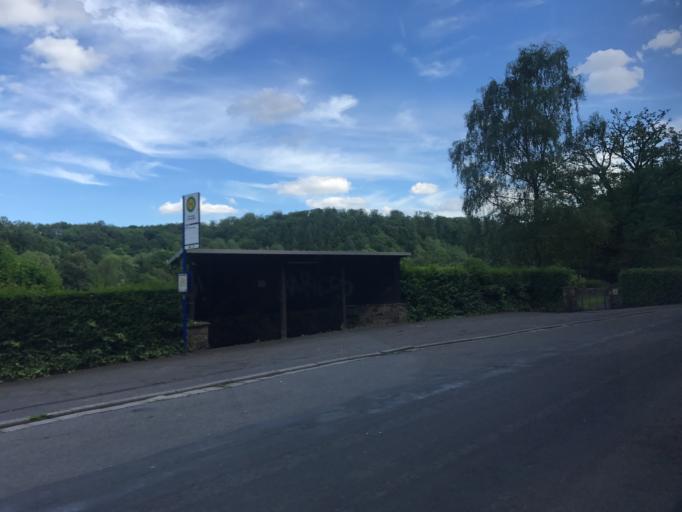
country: DE
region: Hesse
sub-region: Regierungsbezirk Darmstadt
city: Schlangenbad
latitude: 50.0861
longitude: 8.1090
